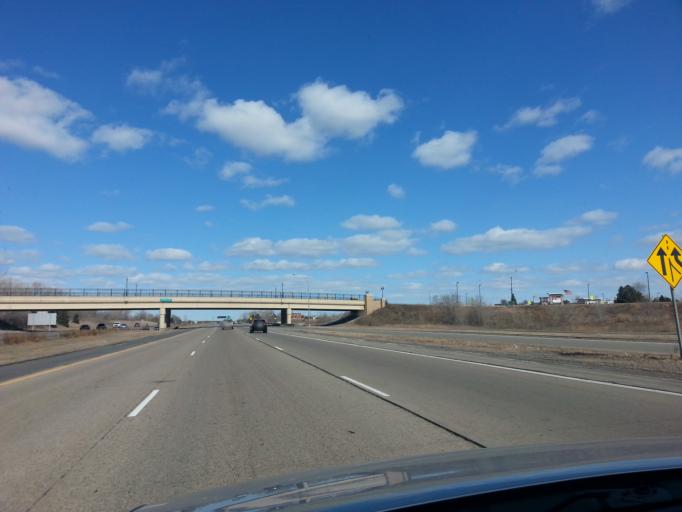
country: US
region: Minnesota
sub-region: Dakota County
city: Eagan
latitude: 44.8362
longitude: -93.1618
